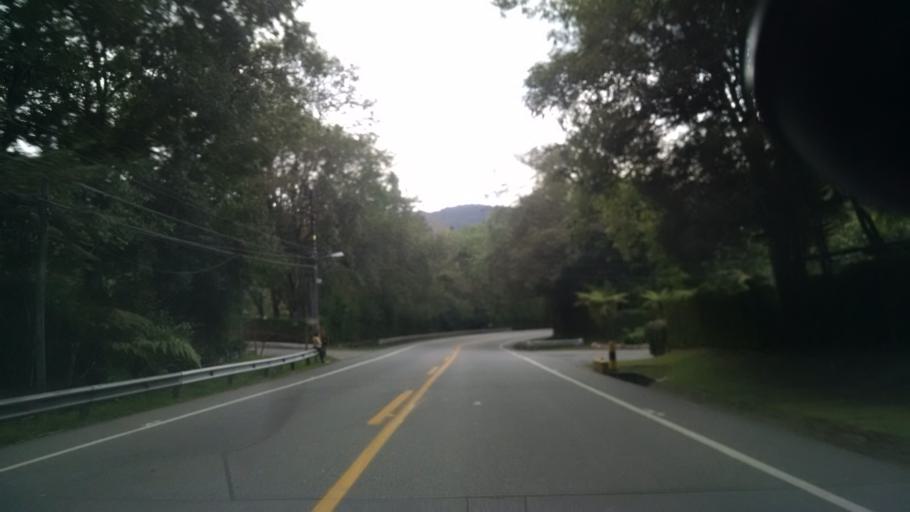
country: CO
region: Antioquia
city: El Retiro
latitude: 6.0980
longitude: -75.5045
